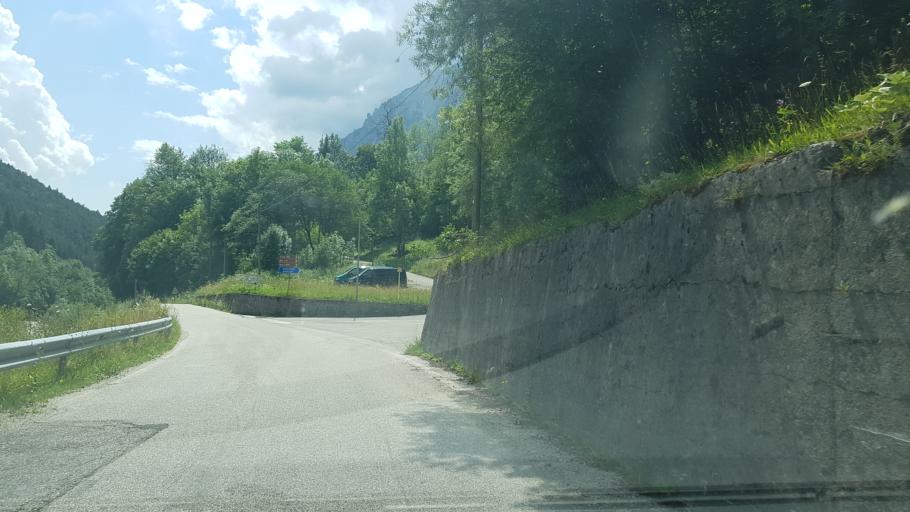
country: IT
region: Friuli Venezia Giulia
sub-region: Provincia di Udine
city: Moggio Udinese
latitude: 46.4885
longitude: 13.1949
